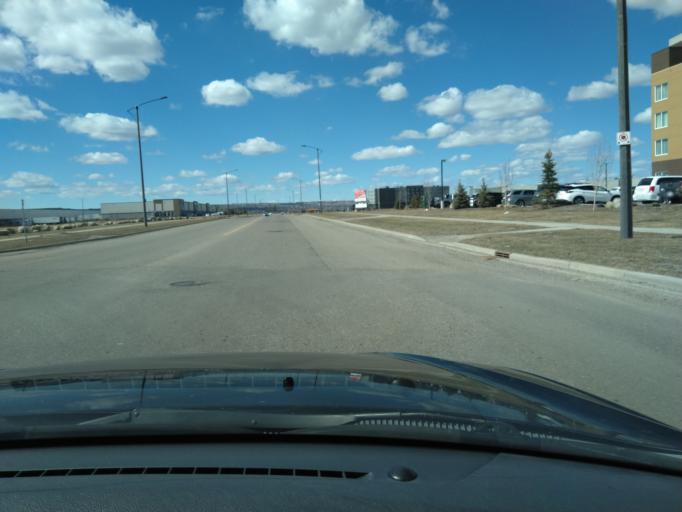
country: CA
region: Alberta
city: Calgary
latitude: 51.1365
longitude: -114.0282
